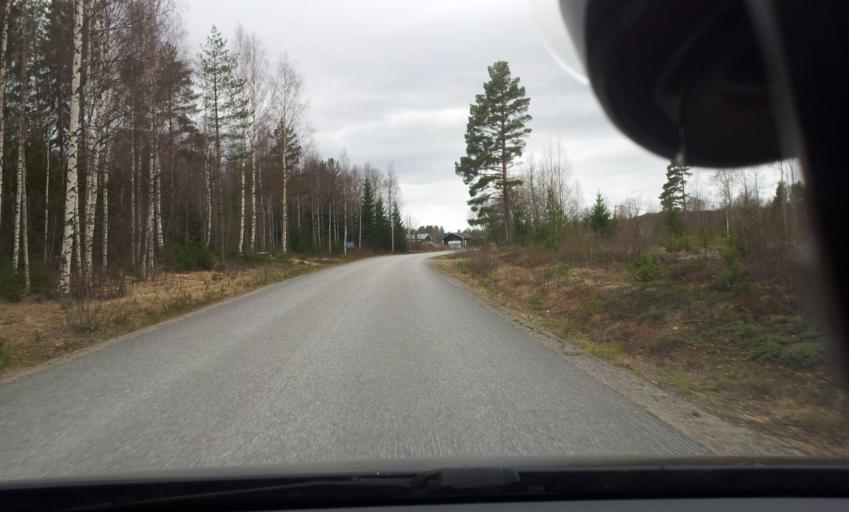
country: SE
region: Gaevleborg
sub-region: Ljusdals Kommun
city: Farila
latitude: 61.8205
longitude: 15.9565
